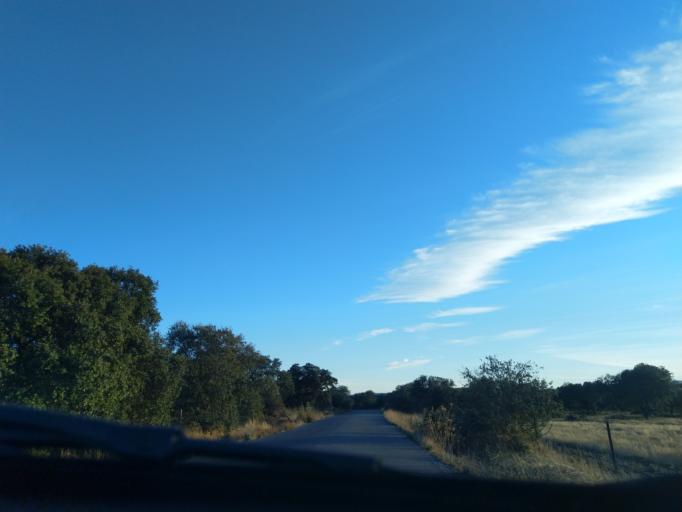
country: ES
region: Extremadura
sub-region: Provincia de Badajoz
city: Valverde de Llerena
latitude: 38.2424
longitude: -5.8244
